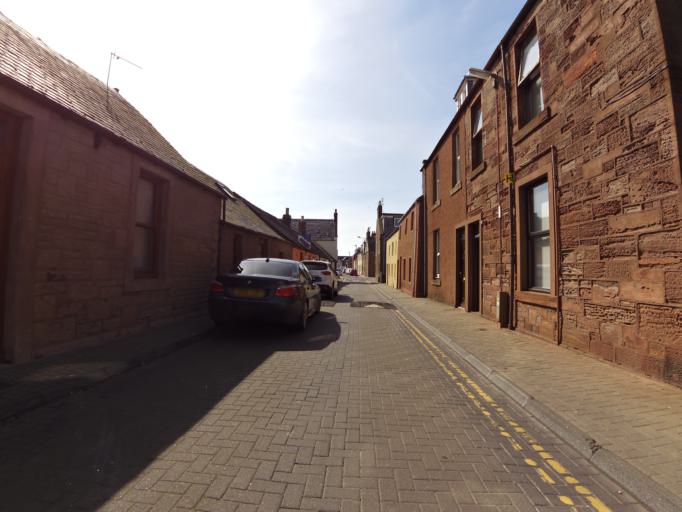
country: GB
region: Scotland
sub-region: Angus
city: Arbroath
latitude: 56.5567
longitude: -2.5791
